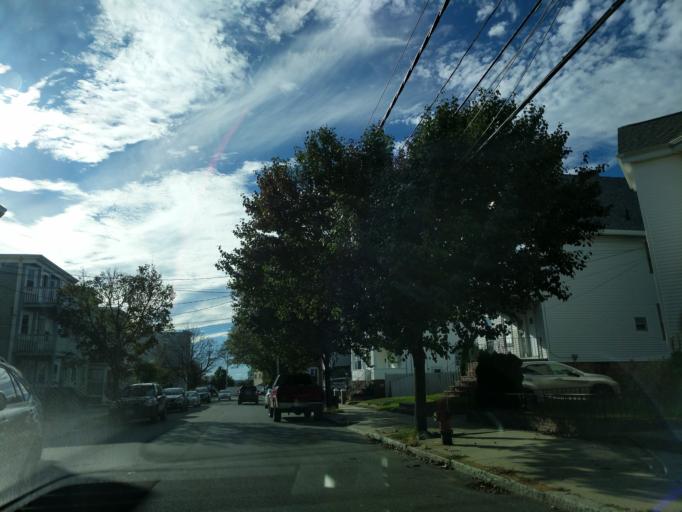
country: US
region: Massachusetts
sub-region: Middlesex County
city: Malden
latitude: 42.4155
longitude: -71.0632
